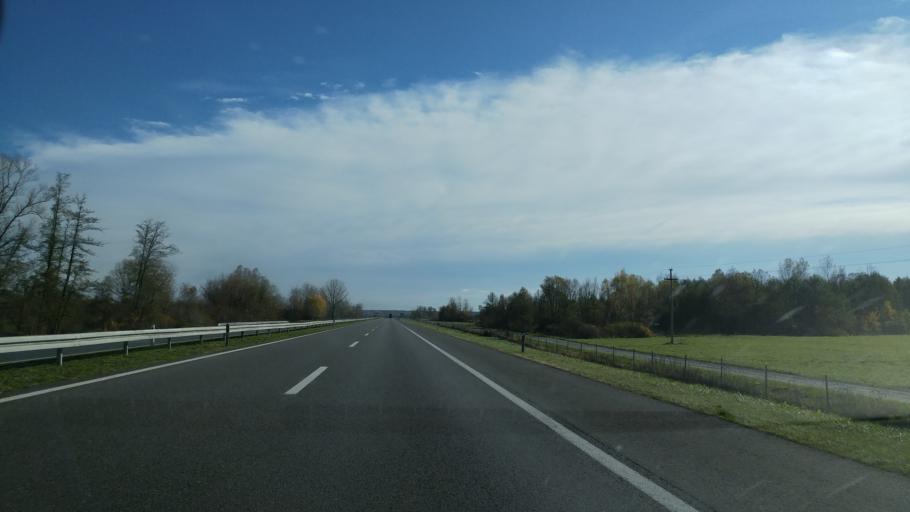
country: HR
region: Brodsko-Posavska
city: Okucani
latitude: 45.2436
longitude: 17.1867
